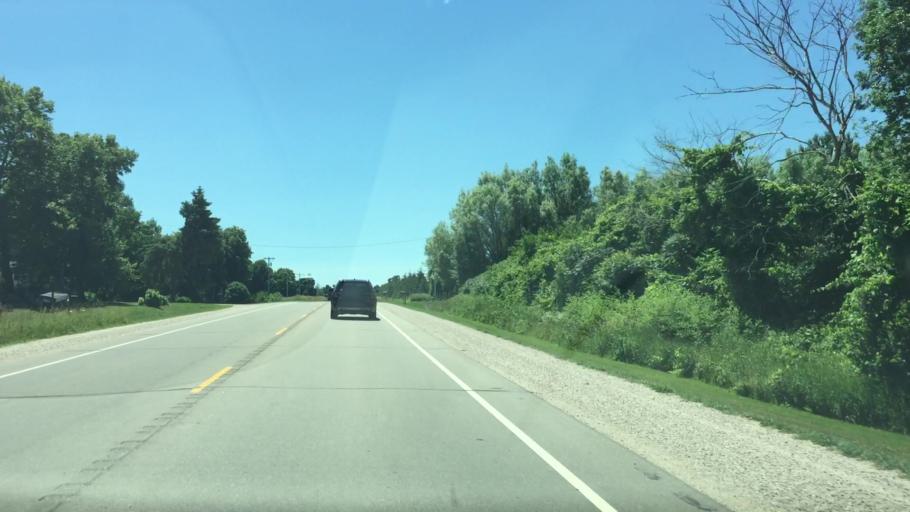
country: US
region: Wisconsin
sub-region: Calumet County
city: New Holstein
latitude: 43.9695
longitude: -88.1124
